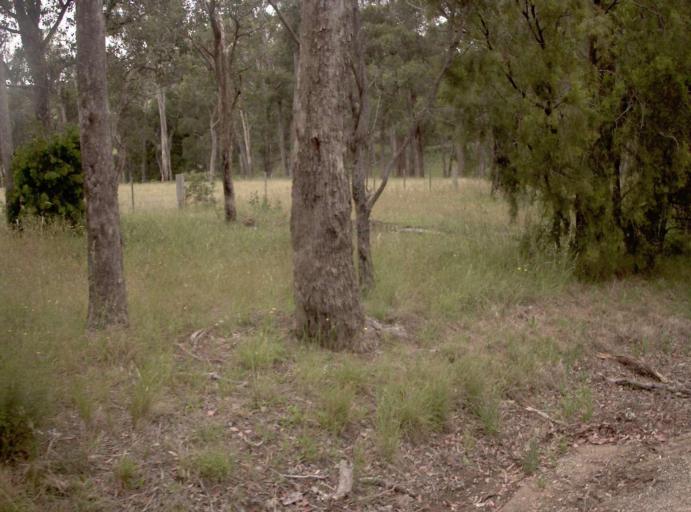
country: AU
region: Victoria
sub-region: East Gippsland
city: Bairnsdale
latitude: -37.7595
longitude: 147.5985
